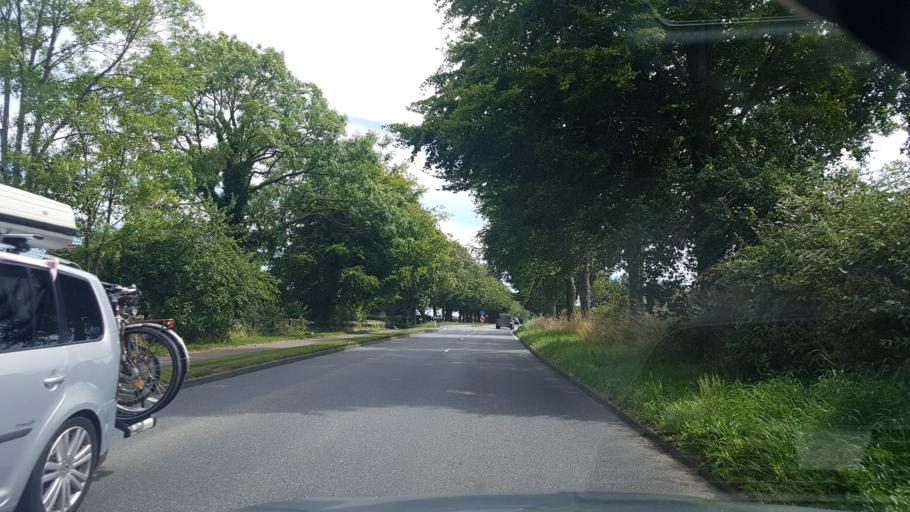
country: DE
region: Schleswig-Holstein
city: Gross Buchwald
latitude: 54.1636
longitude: 10.0933
